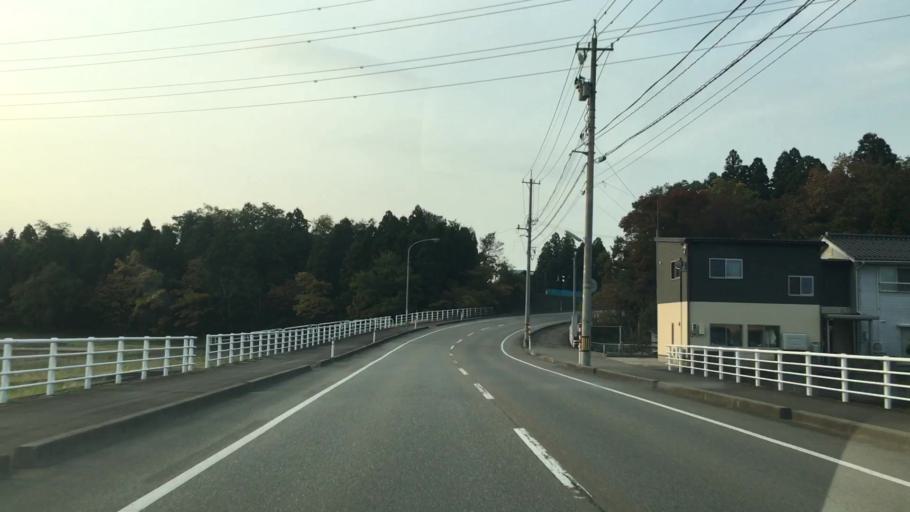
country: JP
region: Toyama
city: Yatsuomachi-higashikumisaka
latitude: 36.5687
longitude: 137.1979
